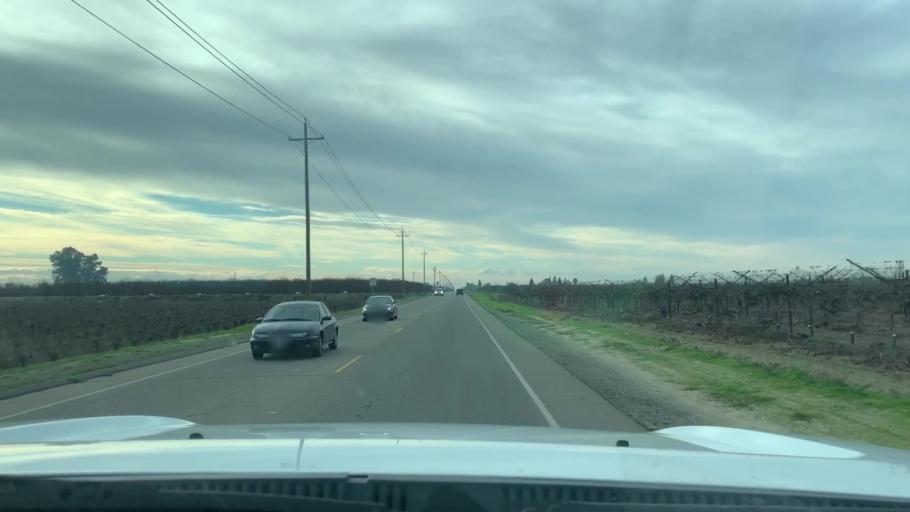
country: US
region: California
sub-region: Fresno County
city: Fowler
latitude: 36.6054
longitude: -119.6672
